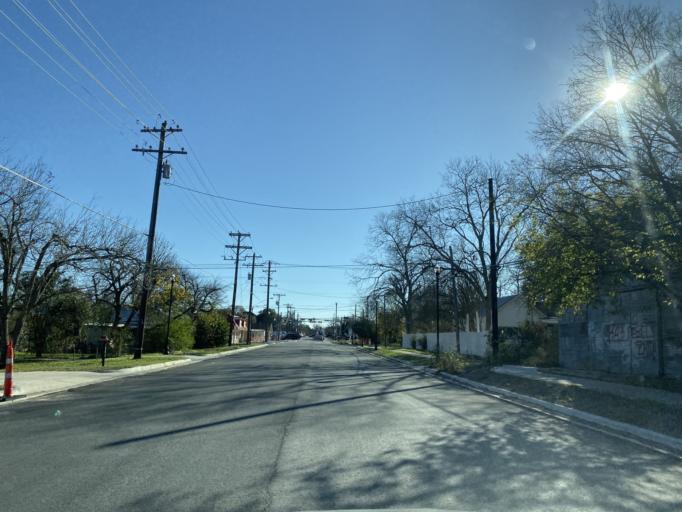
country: US
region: Texas
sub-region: Hays County
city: Kyle
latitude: 29.9905
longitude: -97.8770
